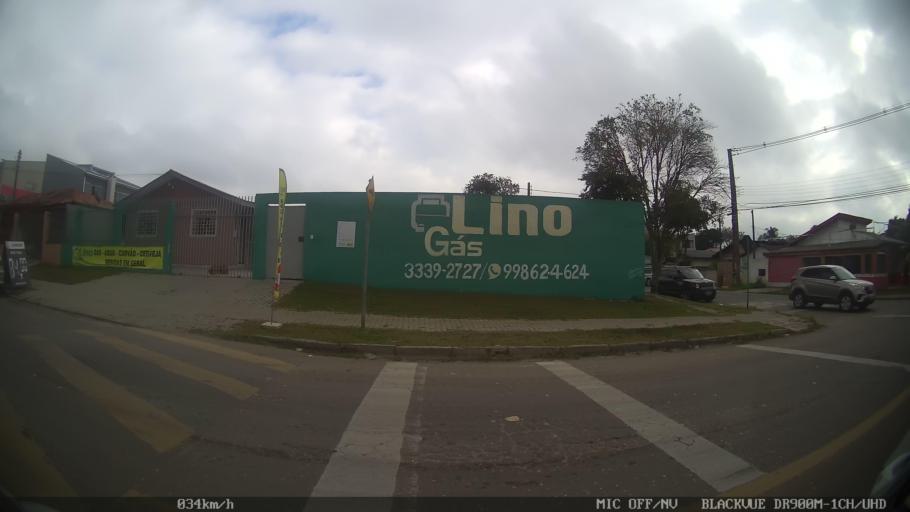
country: BR
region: Parana
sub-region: Curitiba
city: Curitiba
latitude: -25.3689
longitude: -49.2679
